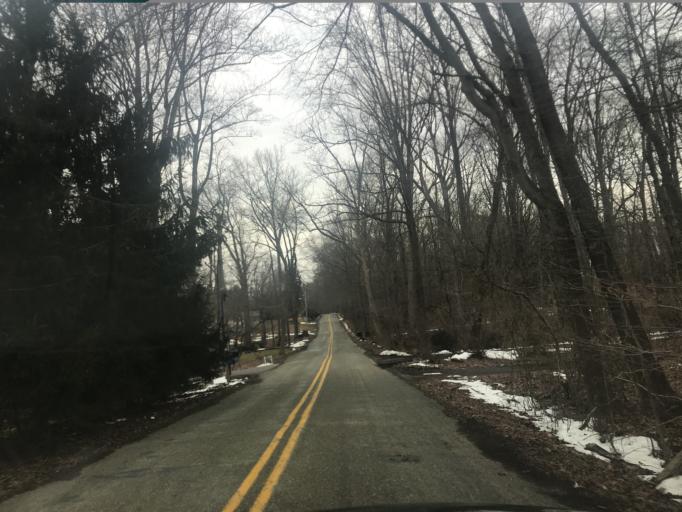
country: US
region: Maryland
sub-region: Harford County
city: Jarrettsville
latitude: 39.6517
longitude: -76.4063
